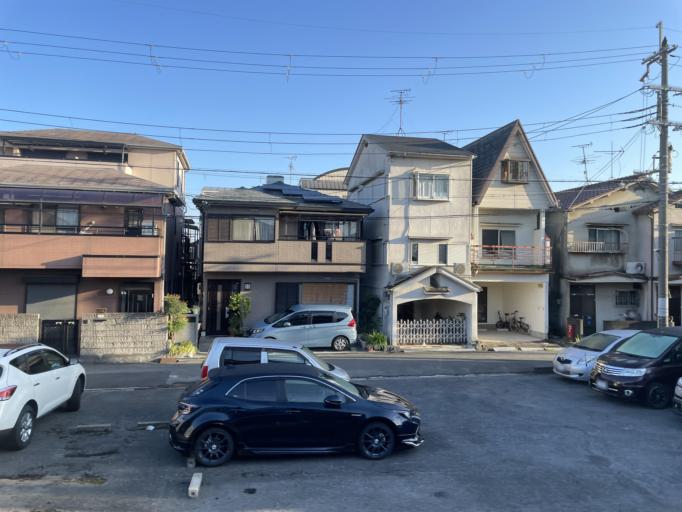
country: JP
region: Osaka
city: Kashihara
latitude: 34.5708
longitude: 135.6015
